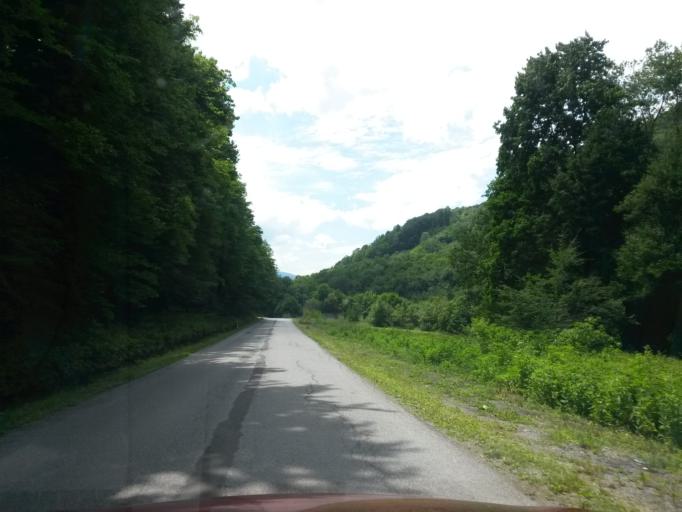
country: SK
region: Kosicky
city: Gelnica
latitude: 48.9147
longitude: 21.0312
